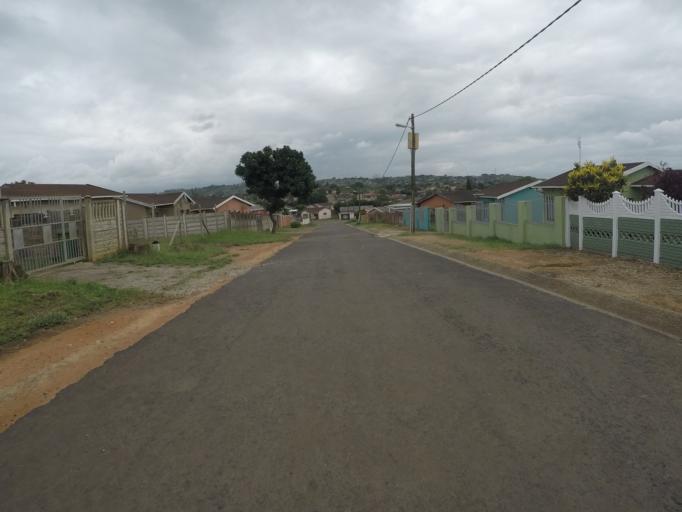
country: ZA
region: KwaZulu-Natal
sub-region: uThungulu District Municipality
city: Empangeni
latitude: -28.7838
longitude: 31.8507
